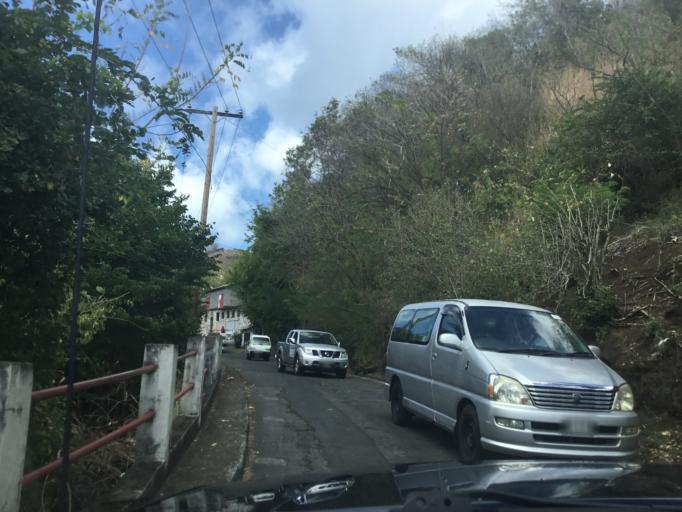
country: VC
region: Saint George
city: Kingstown Park
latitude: 13.1573
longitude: -61.2329
